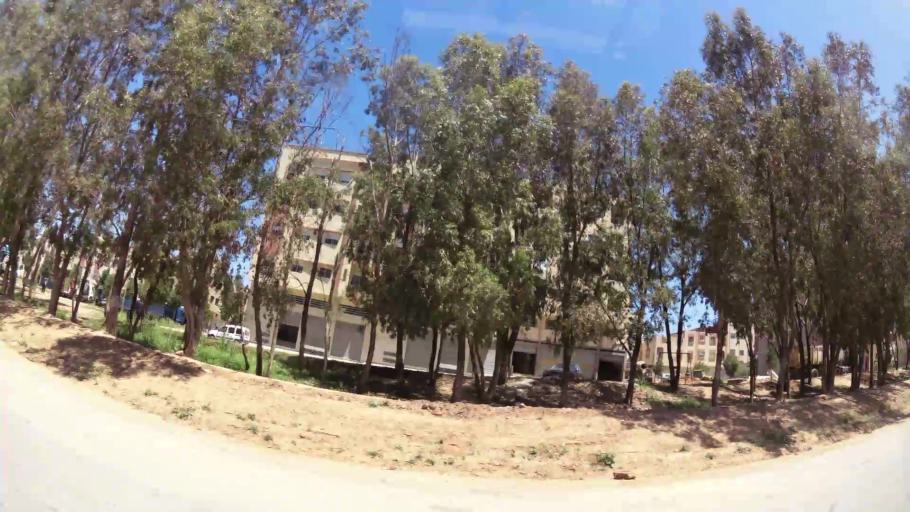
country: MA
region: Meknes-Tafilalet
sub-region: Meknes
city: Meknes
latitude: 33.8500
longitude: -5.5598
